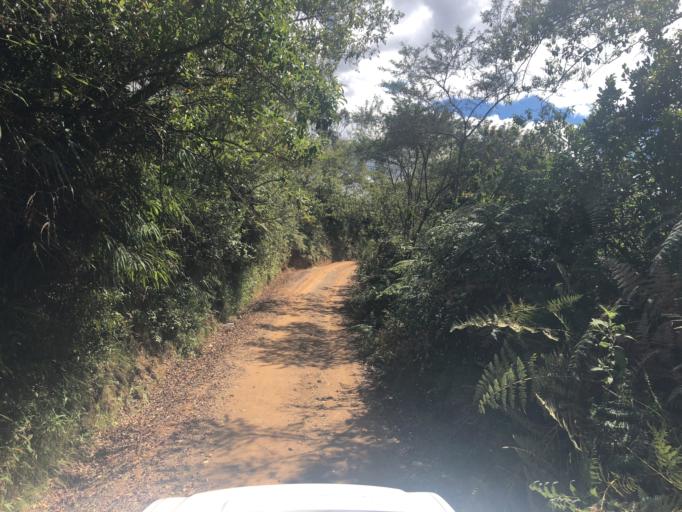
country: CO
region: Cauca
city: Silvia
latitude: 2.6807
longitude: -76.4381
